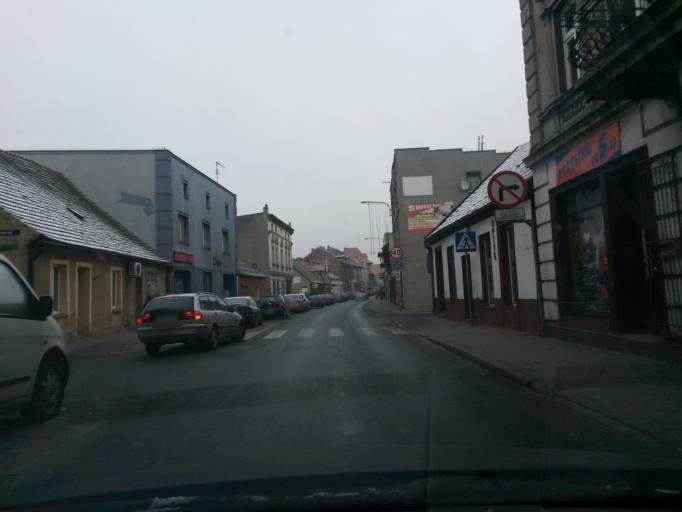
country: PL
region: Kujawsko-Pomorskie
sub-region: Powiat mogilenski
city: Strzelno
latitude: 52.6288
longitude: 18.1733
